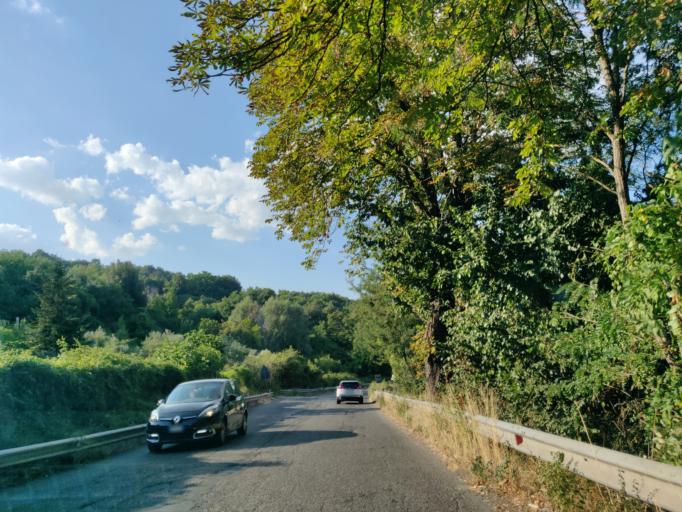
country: IT
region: Latium
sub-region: Provincia di Viterbo
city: Acquapendente
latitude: 42.7512
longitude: 11.8648
